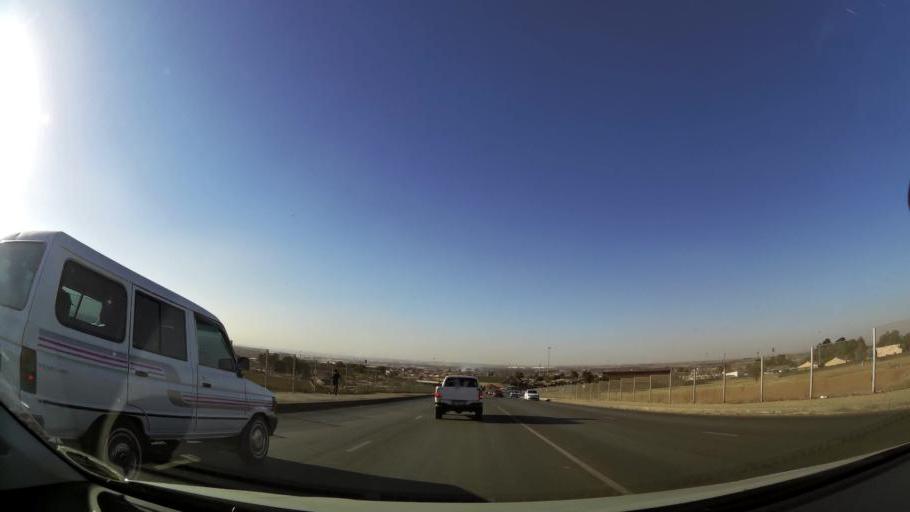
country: ZA
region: Gauteng
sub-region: Ekurhuleni Metropolitan Municipality
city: Tembisa
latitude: -26.0026
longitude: 28.2215
